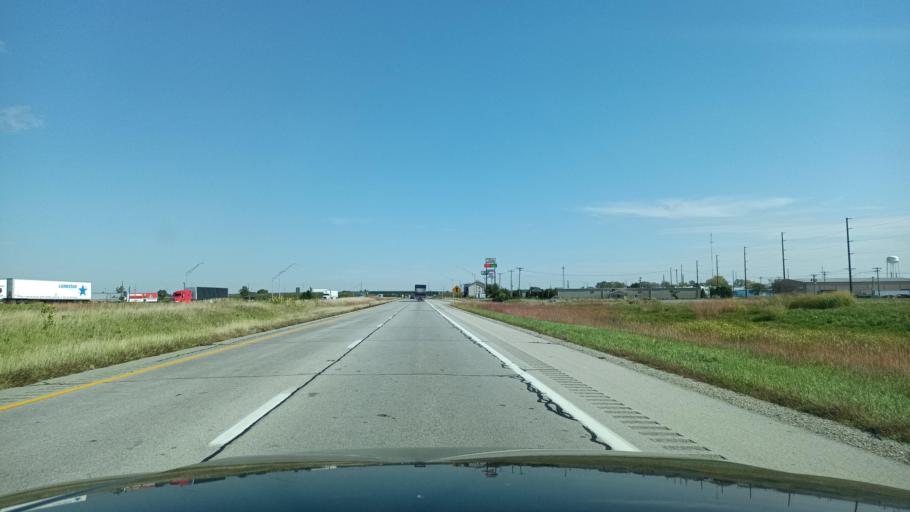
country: US
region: Ohio
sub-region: Henry County
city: Napoleon
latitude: 41.4144
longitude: -84.1038
